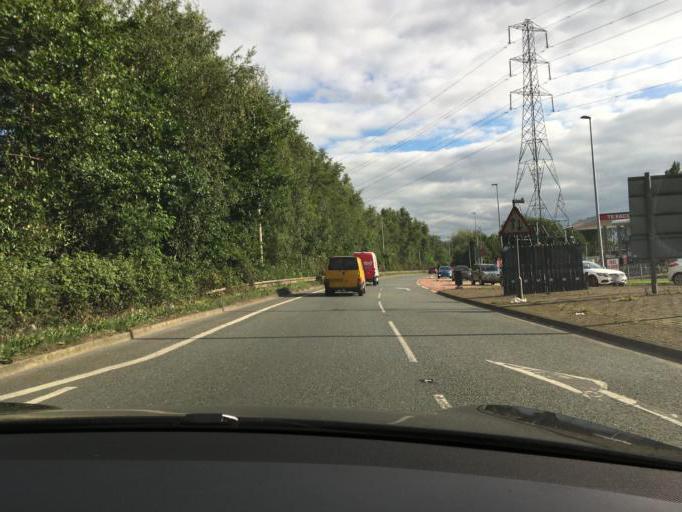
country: GB
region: England
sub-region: City and Borough of Salford
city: Irlam
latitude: 53.4571
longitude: -2.4005
